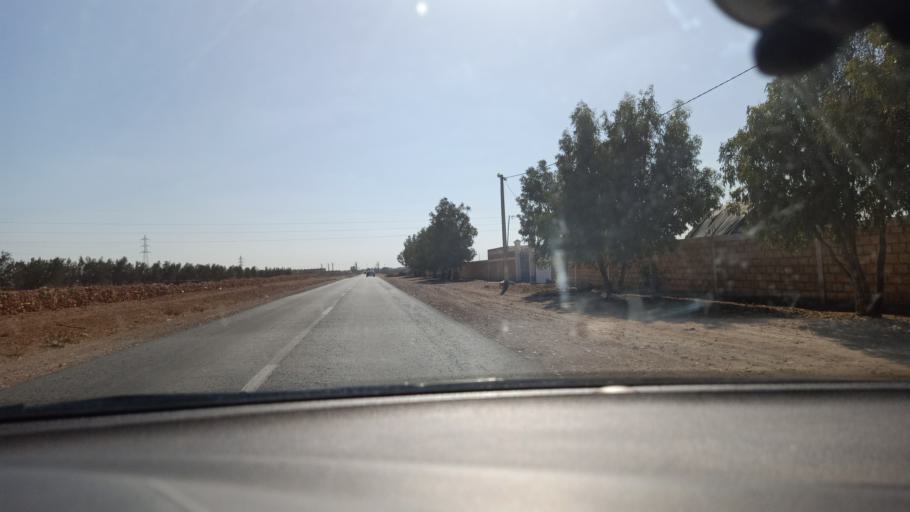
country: MA
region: Doukkala-Abda
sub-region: Safi
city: Youssoufia
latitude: 32.1161
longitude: -8.6060
